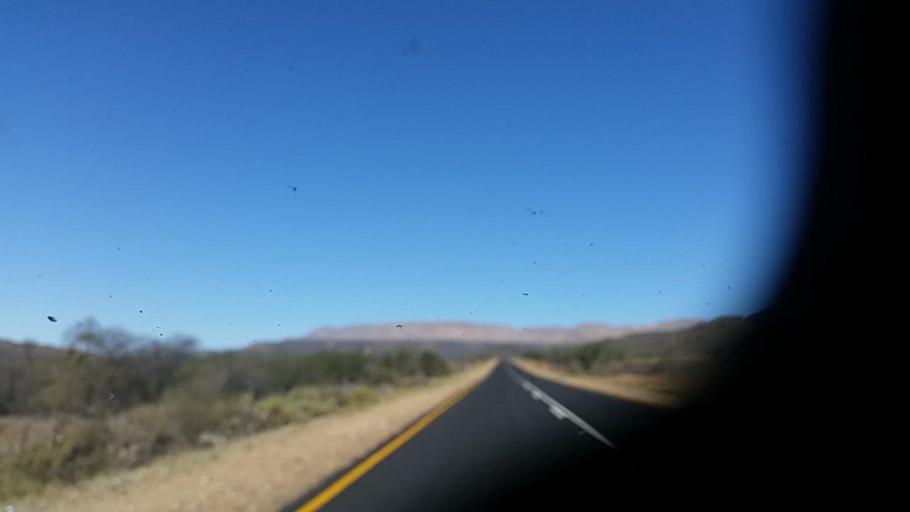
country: ZA
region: Western Cape
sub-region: Eden District Municipality
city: George
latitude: -33.5411
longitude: 22.7264
